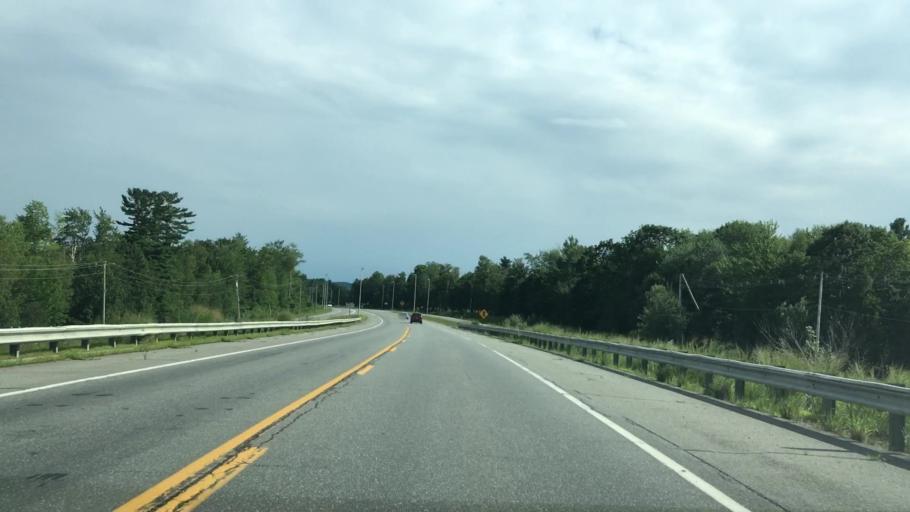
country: US
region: Maine
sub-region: Waldo County
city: Belfast
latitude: 44.4227
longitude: -69.0214
